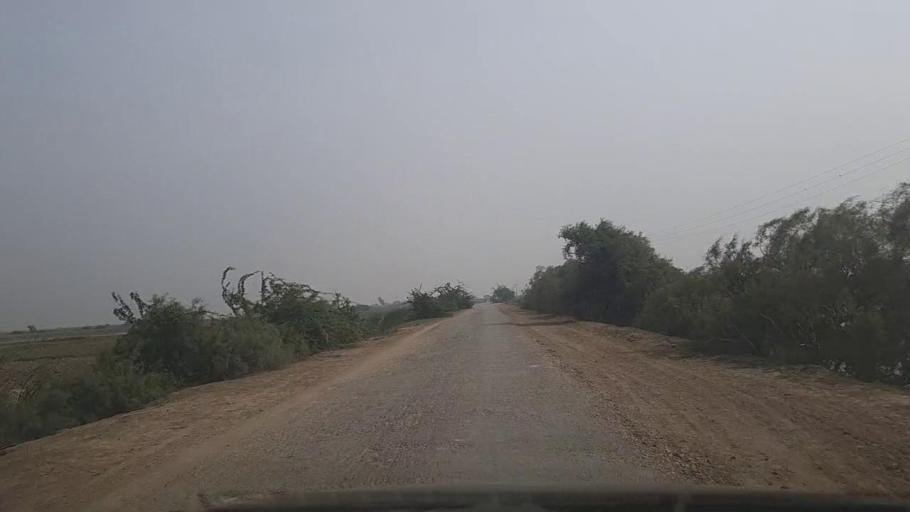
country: PK
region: Sindh
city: Mirpur Sakro
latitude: 24.4767
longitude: 67.6632
